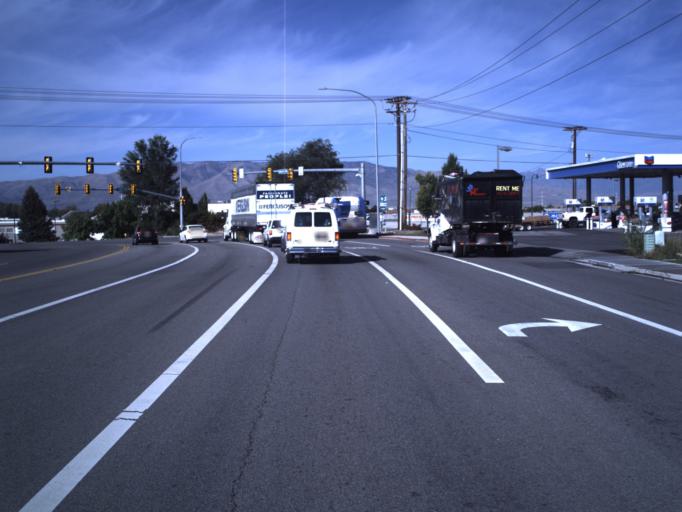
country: US
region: Utah
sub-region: Utah County
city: Orem
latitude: 40.2753
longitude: -111.7261
